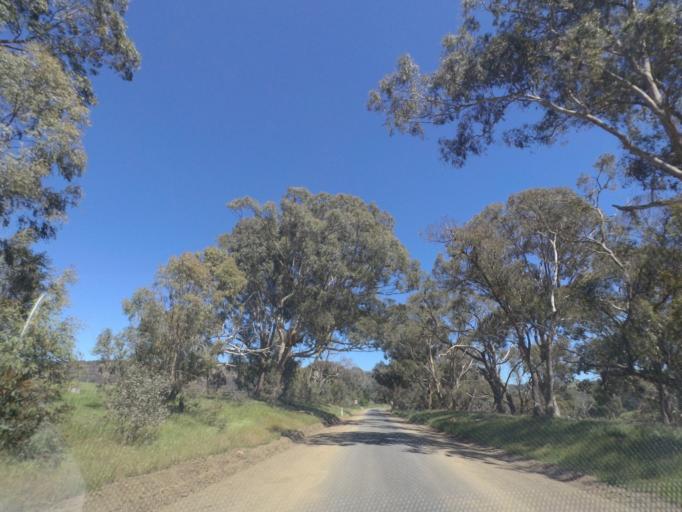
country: AU
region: Victoria
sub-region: Whittlesea
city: Whittlesea
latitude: -37.2900
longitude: 144.9896
